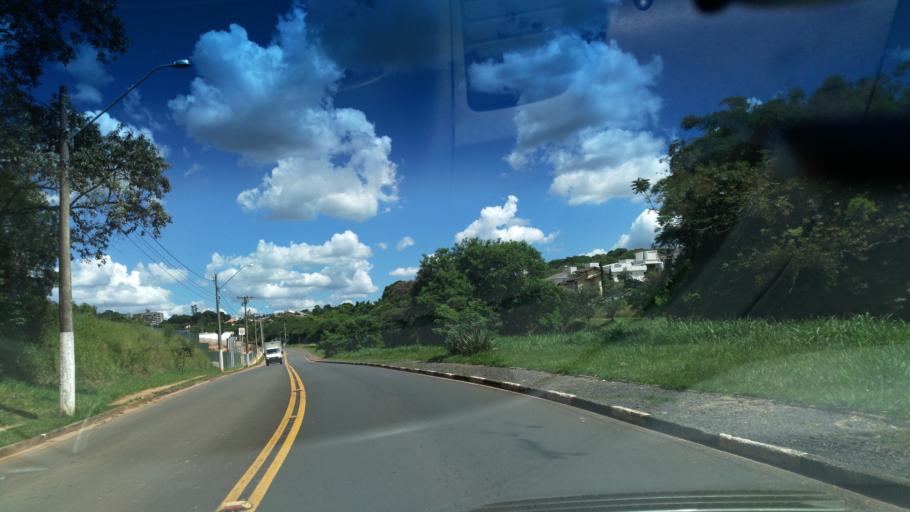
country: BR
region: Sao Paulo
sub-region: Valinhos
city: Valinhos
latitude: -22.9735
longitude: -47.0144
